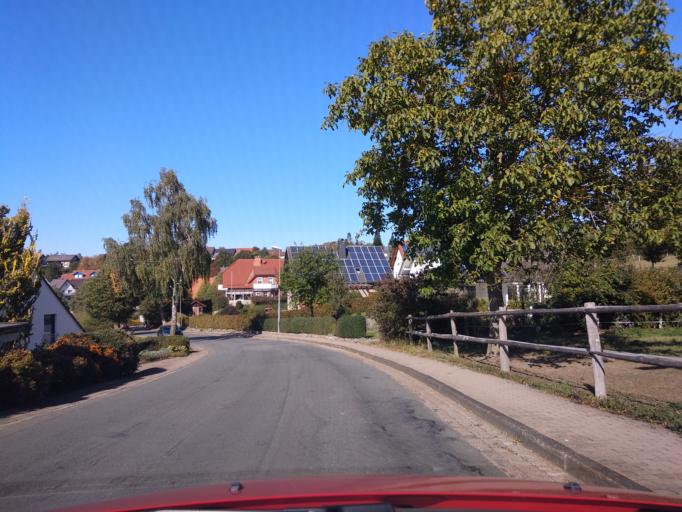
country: DE
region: Lower Saxony
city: Boffzen
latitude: 51.7495
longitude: 9.3069
